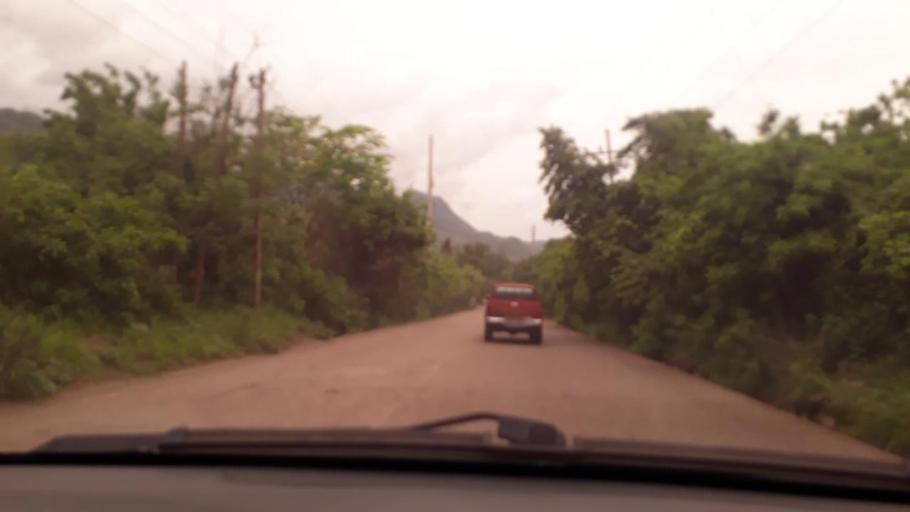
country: GT
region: Chiquimula
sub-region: Municipio de Jocotan
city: Jocotan
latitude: 14.7976
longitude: -89.3952
